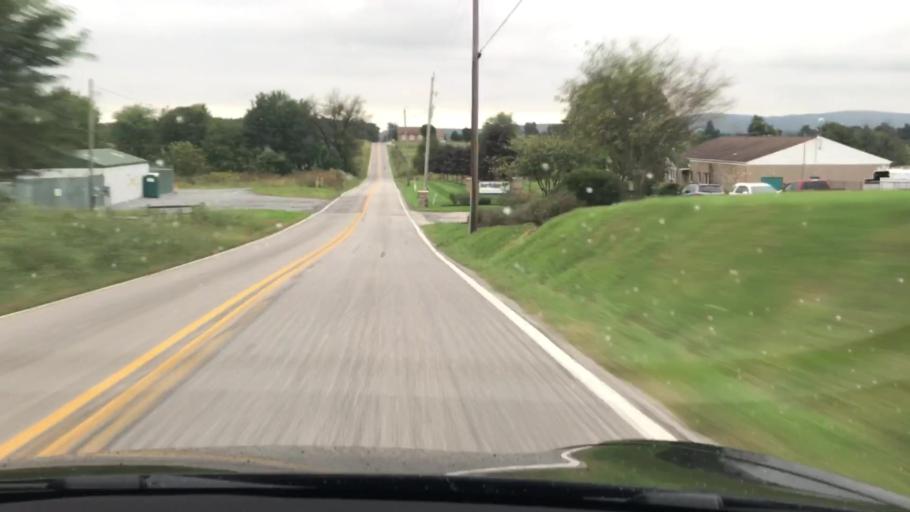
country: US
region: Pennsylvania
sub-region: York County
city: Dover
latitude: 39.9658
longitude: -76.8739
